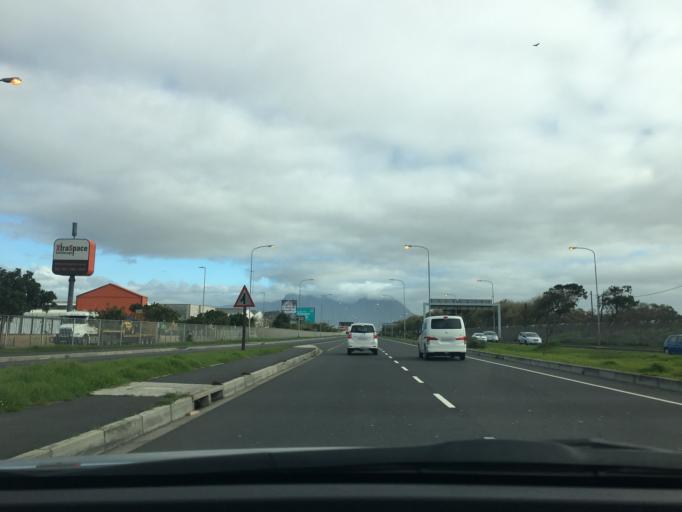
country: ZA
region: Western Cape
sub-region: City of Cape Town
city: Lansdowne
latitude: -33.9685
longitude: 18.5867
